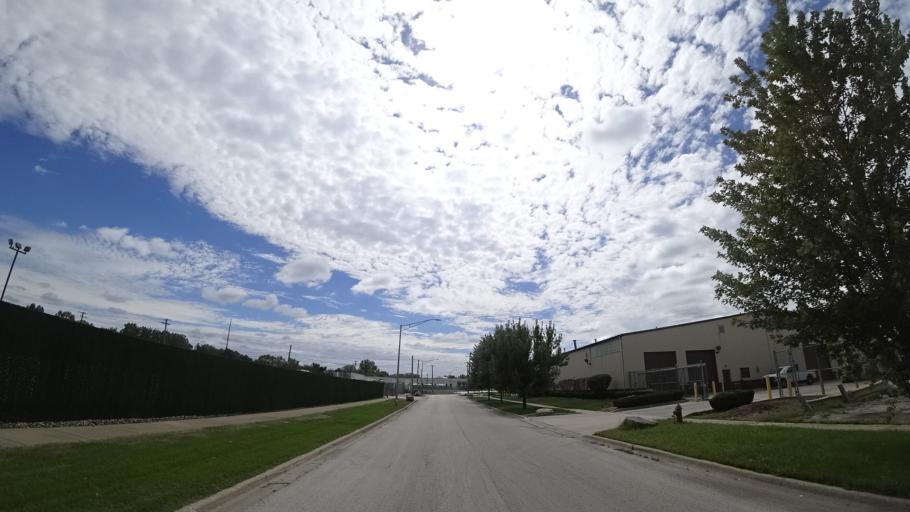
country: US
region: Illinois
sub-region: Cook County
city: Chicago Ridge
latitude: 41.7078
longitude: -87.7890
